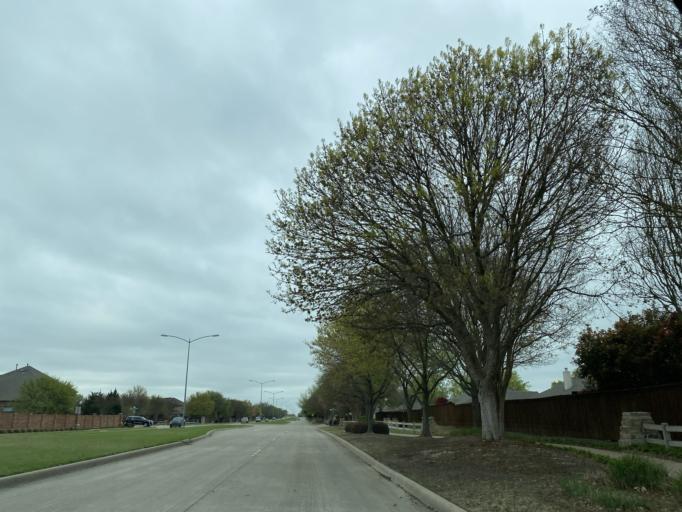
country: US
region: Texas
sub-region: Collin County
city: Fairview
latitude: 33.1238
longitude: -96.6288
